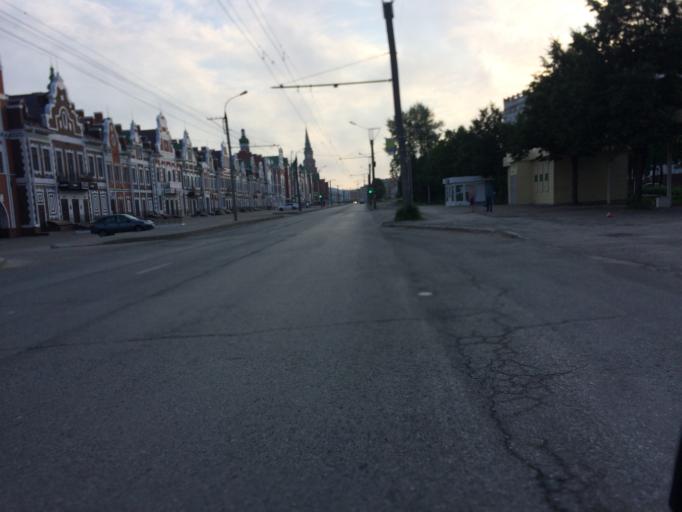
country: RU
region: Mariy-El
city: Yoshkar-Ola
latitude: 56.6292
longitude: 47.9059
